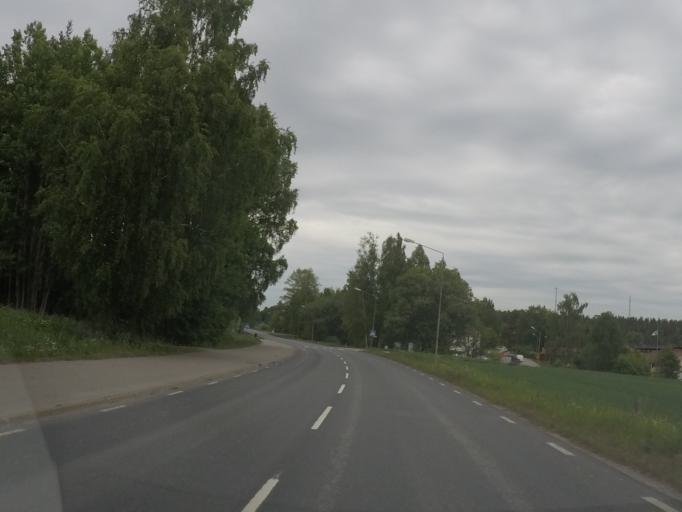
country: SE
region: Soedermanland
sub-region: Eskilstuna Kommun
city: Arla
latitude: 59.2791
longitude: 16.6706
